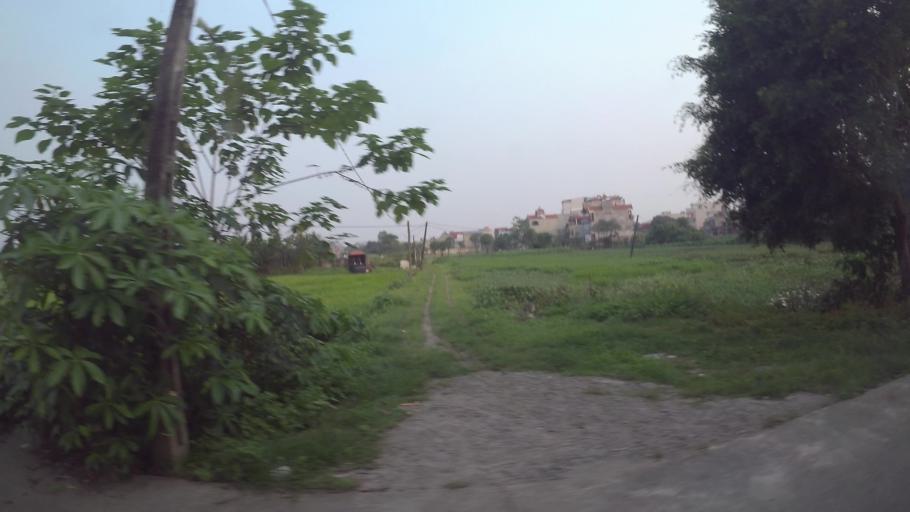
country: VN
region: Ha Noi
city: Thuong Tin
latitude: 20.8774
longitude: 105.8625
